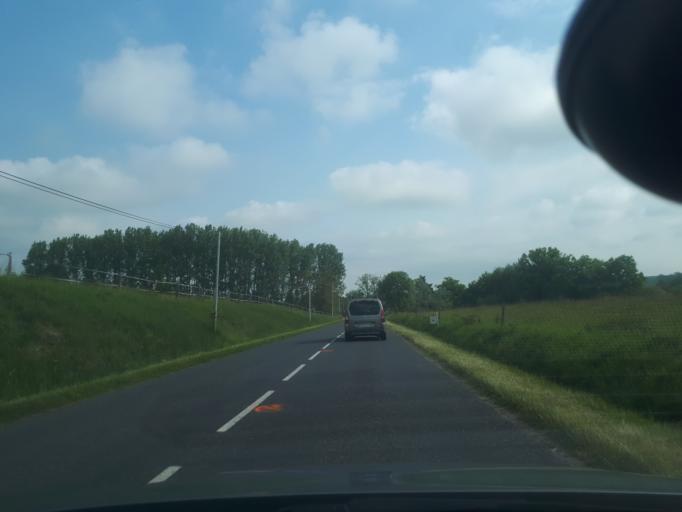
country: FR
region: Auvergne
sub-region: Departement de l'Allier
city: Lapalisse
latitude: 46.3344
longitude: 3.5807
